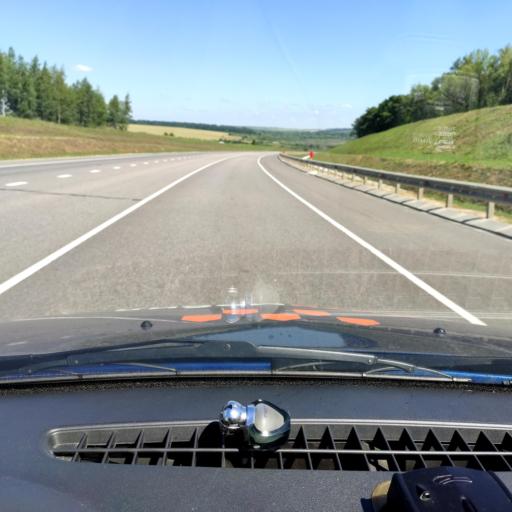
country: RU
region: Orjol
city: Pokrovskoye
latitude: 52.6213
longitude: 36.8621
